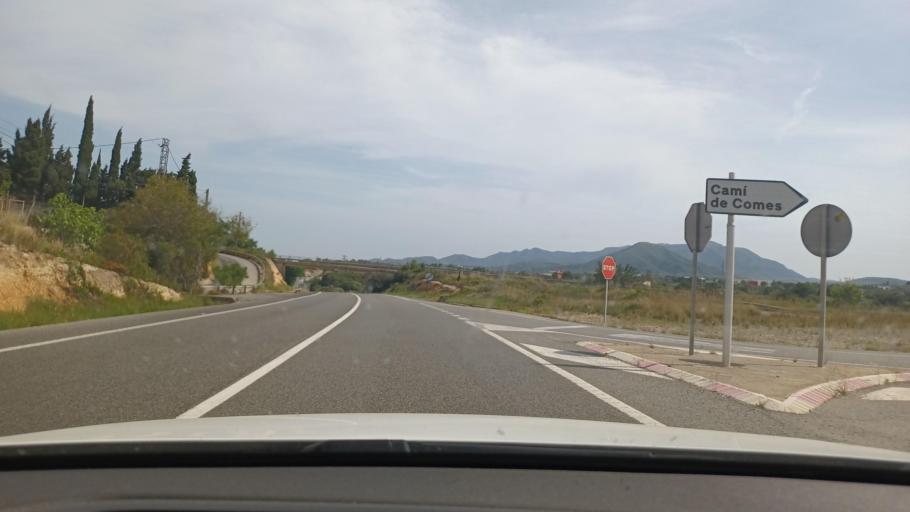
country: ES
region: Catalonia
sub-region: Provincia de Tarragona
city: Amposta
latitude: 40.7169
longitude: 0.5632
